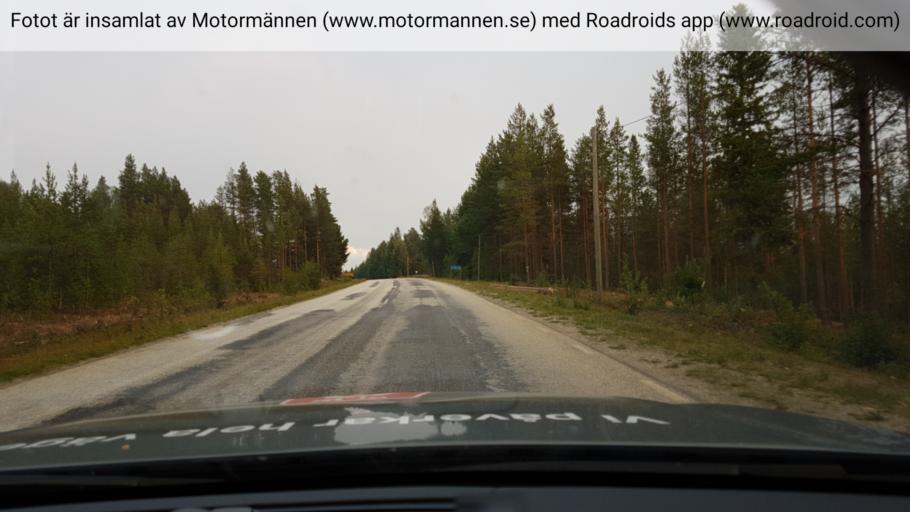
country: SE
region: Jaemtland
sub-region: Harjedalens Kommun
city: Sveg
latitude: 62.4167
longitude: 13.5507
